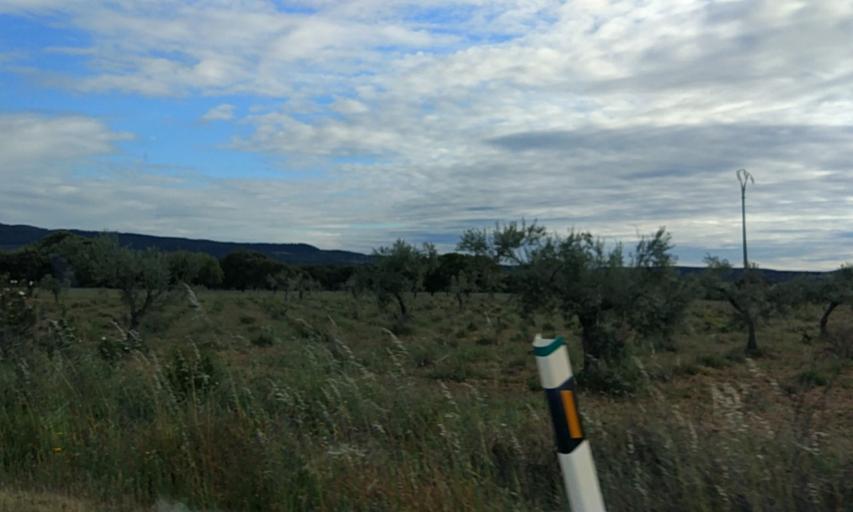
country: ES
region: Extremadura
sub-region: Provincia de Caceres
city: Torrejoncillo
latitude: 39.8718
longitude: -6.4424
